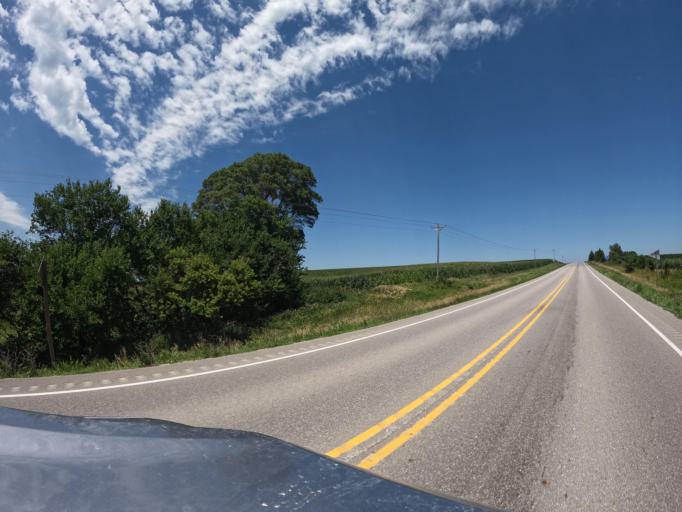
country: US
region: Iowa
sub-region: Keokuk County
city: Sigourney
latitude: 41.4122
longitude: -92.3546
